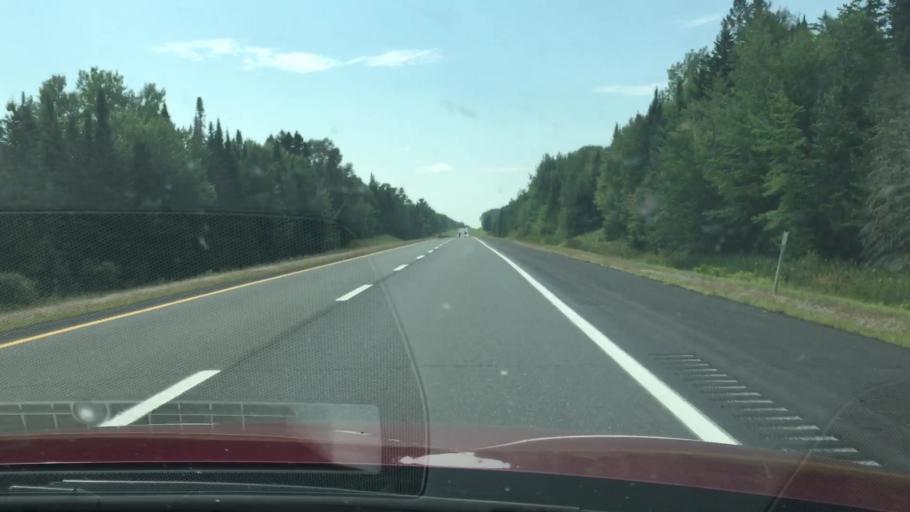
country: US
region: Maine
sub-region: Penobscot County
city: Patten
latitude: 46.0409
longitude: -68.2641
